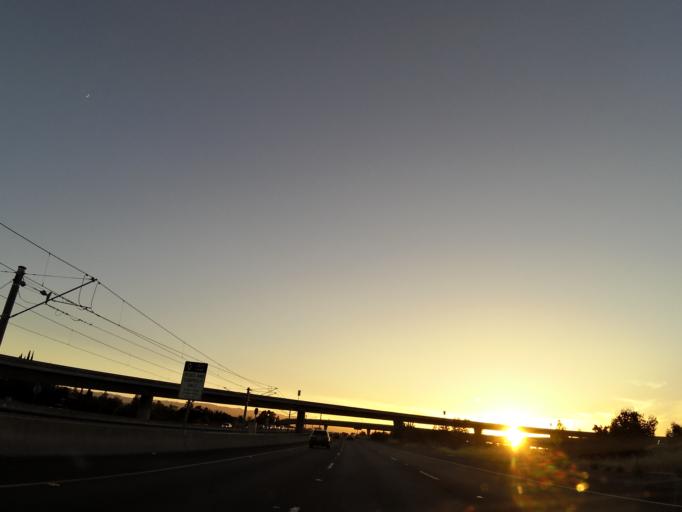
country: US
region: California
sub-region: Santa Clara County
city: Seven Trees
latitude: 37.2556
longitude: -121.8553
